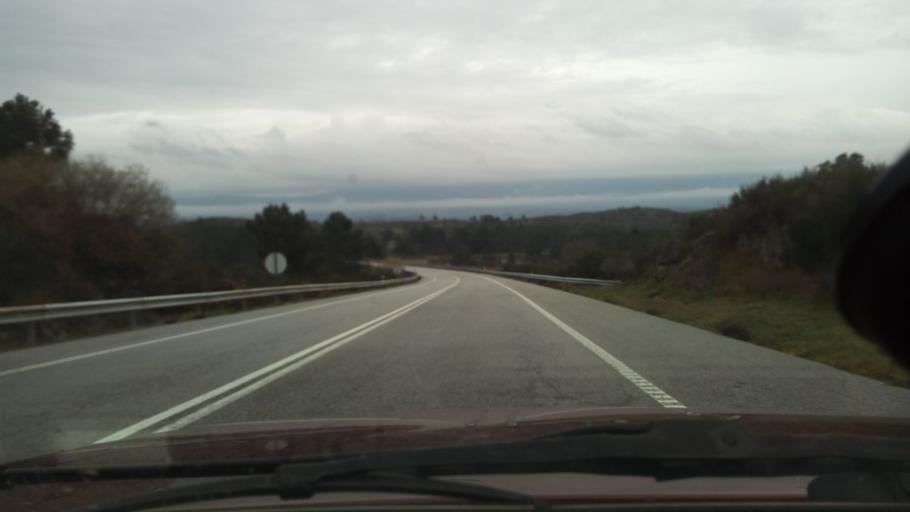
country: PT
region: Guarda
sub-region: Fornos de Algodres
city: Fornos de Algodres
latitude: 40.6038
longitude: -7.5830
